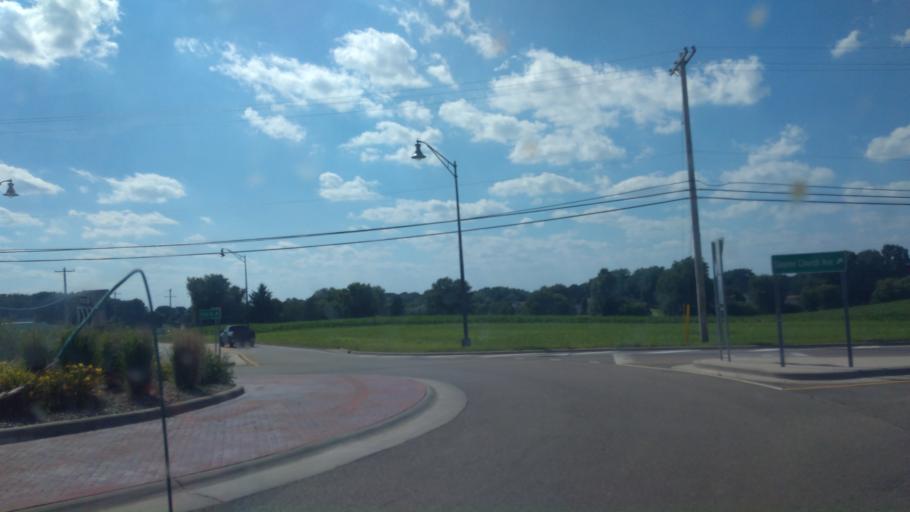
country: US
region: Ohio
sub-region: Stark County
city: Richville
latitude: 40.7306
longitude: -81.4568
